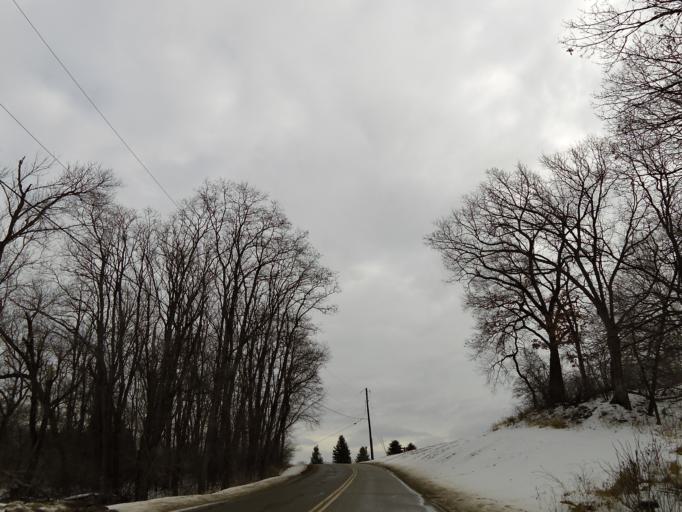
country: US
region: Minnesota
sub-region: Washington County
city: Bayport
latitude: 44.9948
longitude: -92.7972
